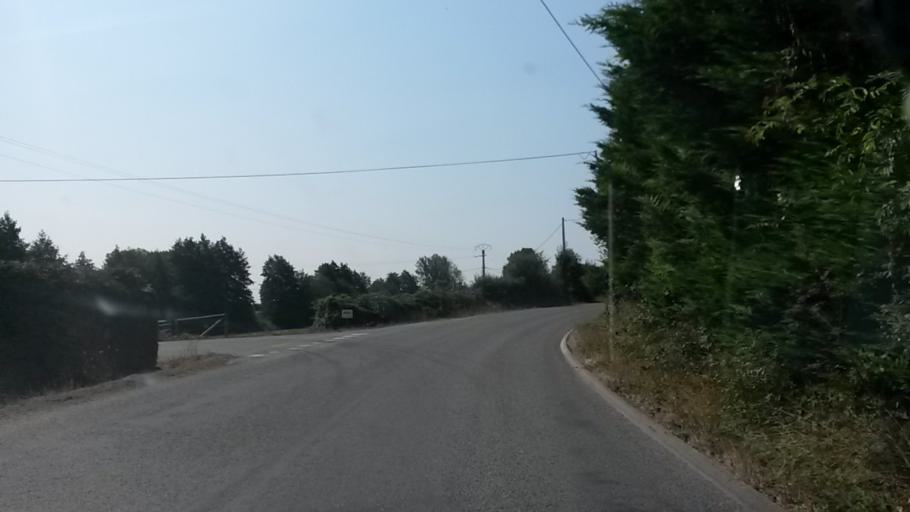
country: FR
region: Pays de la Loire
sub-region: Departement de la Mayenne
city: Saint-Pierre-des-Nids
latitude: 48.3823
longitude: -0.1397
